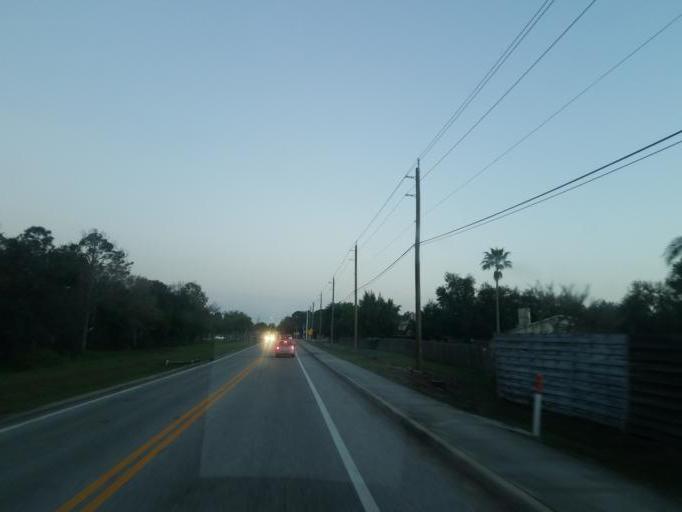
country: US
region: Florida
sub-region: Sarasota County
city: Fruitville
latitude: 27.3420
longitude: -82.4638
